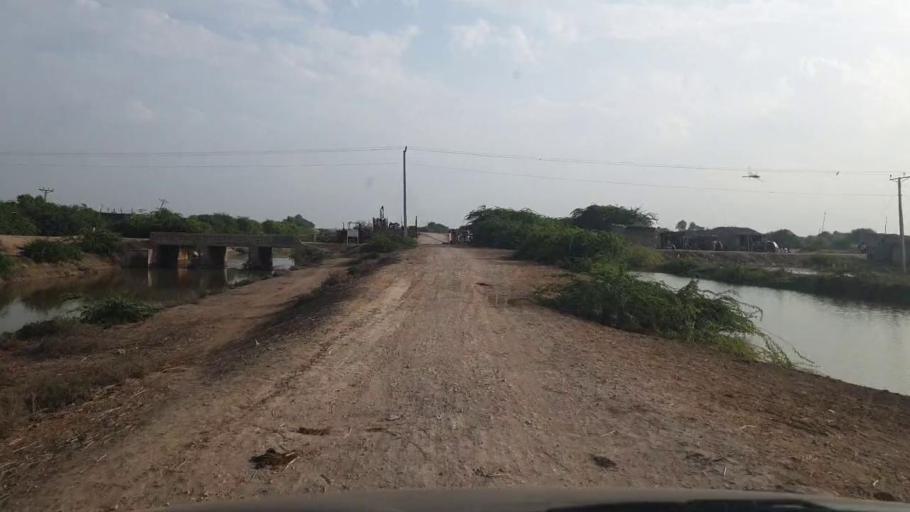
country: PK
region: Sindh
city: Badin
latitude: 24.5501
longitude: 68.6709
